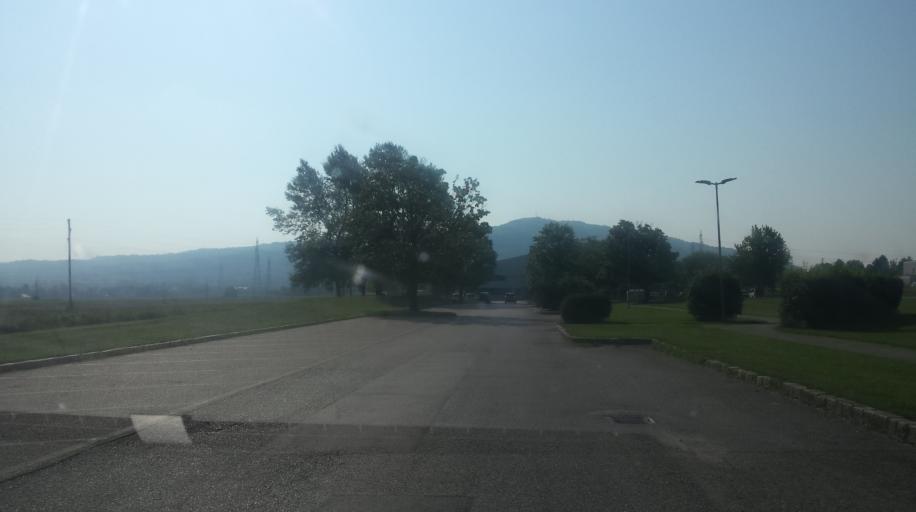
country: AT
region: Lower Austria
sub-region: Politischer Bezirk Korneuburg
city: Bisamberg
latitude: 48.3376
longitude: 16.3425
